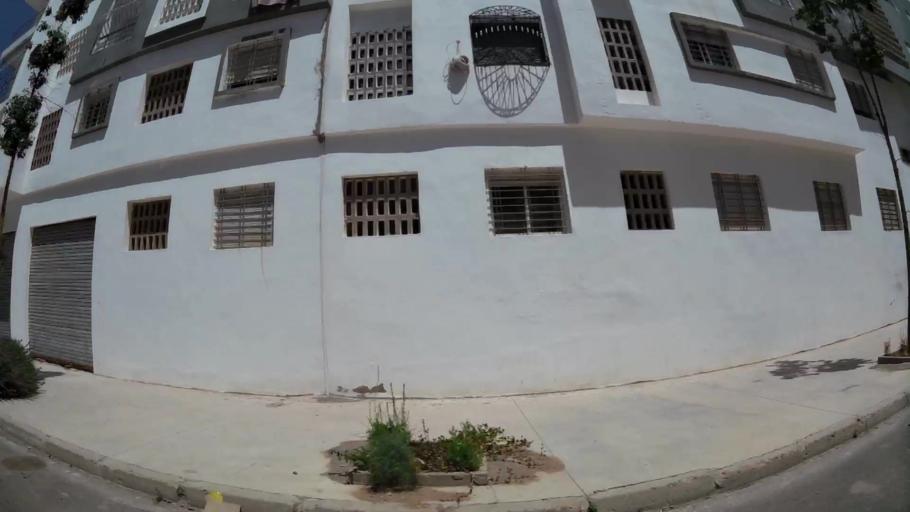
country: MA
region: Oued ed Dahab-Lagouira
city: Dakhla
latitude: 30.4393
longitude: -9.5608
